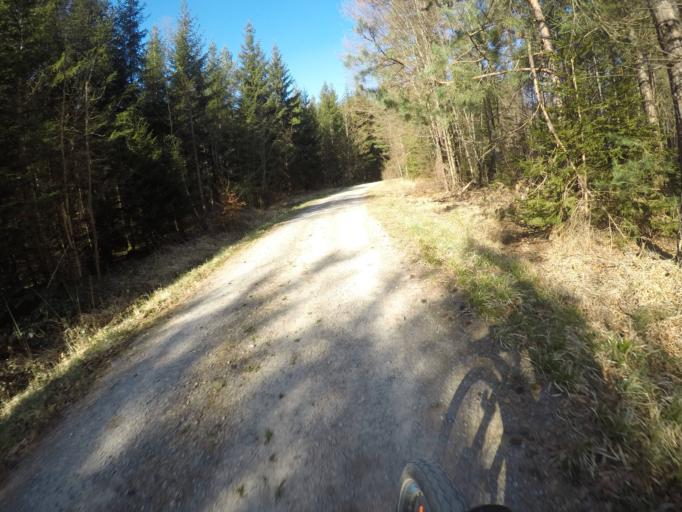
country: DE
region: Baden-Wuerttemberg
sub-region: Tuebingen Region
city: Dettenhausen
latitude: 48.6045
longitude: 9.1224
